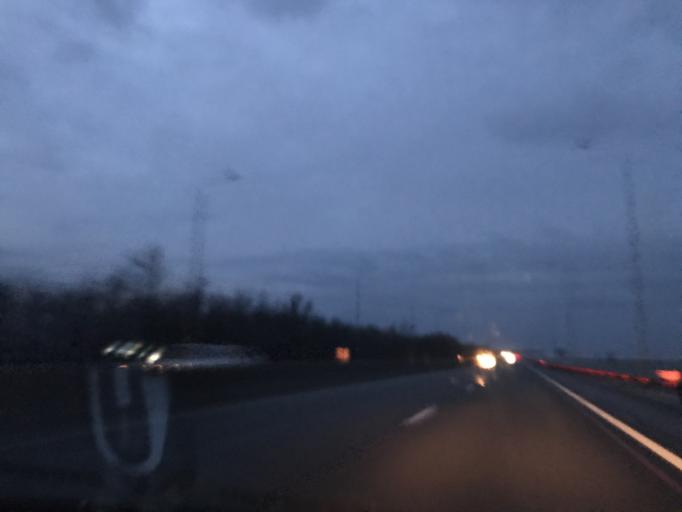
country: RU
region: Rostov
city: Samarskoye
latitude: 46.9744
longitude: 39.7217
